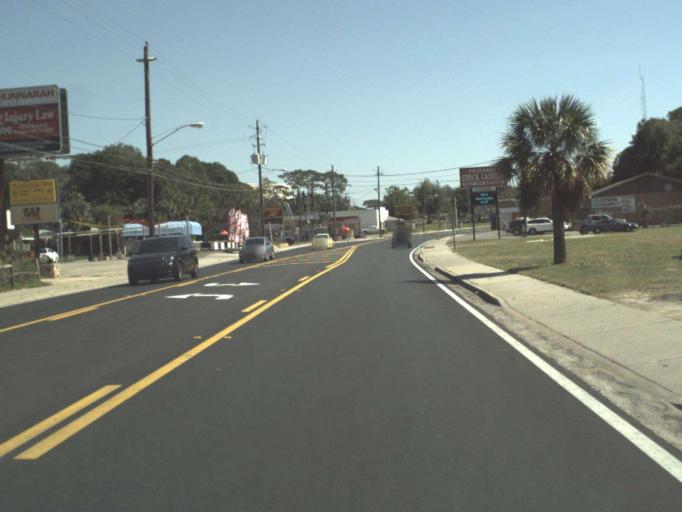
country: US
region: Florida
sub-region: Bay County
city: Panama City
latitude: 30.1587
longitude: -85.6551
